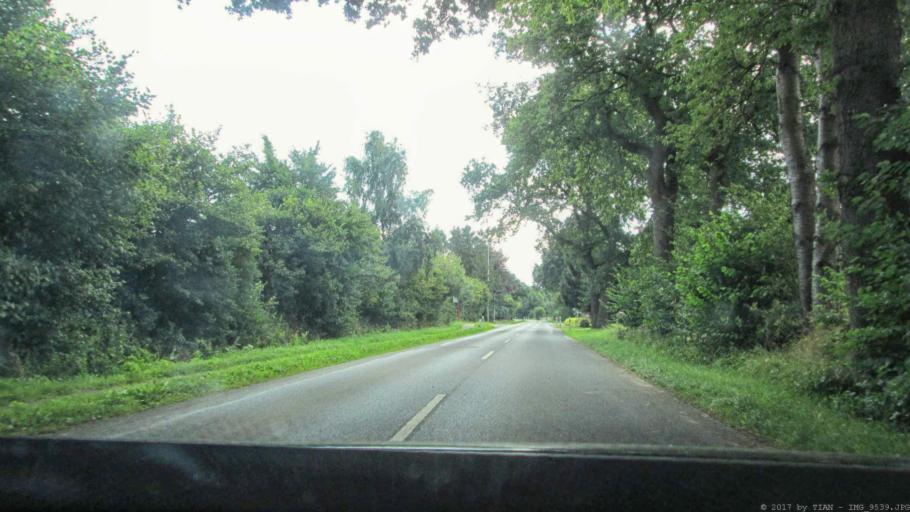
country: DE
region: Schleswig-Holstein
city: Seth
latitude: 53.8317
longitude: 10.1847
